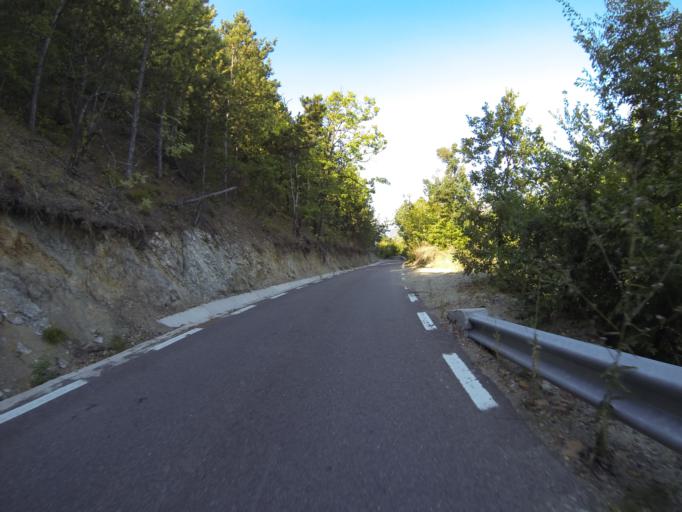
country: RO
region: Mehedinti
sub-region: Comuna Dubova
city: Dubova
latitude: 44.5405
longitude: 22.2092
